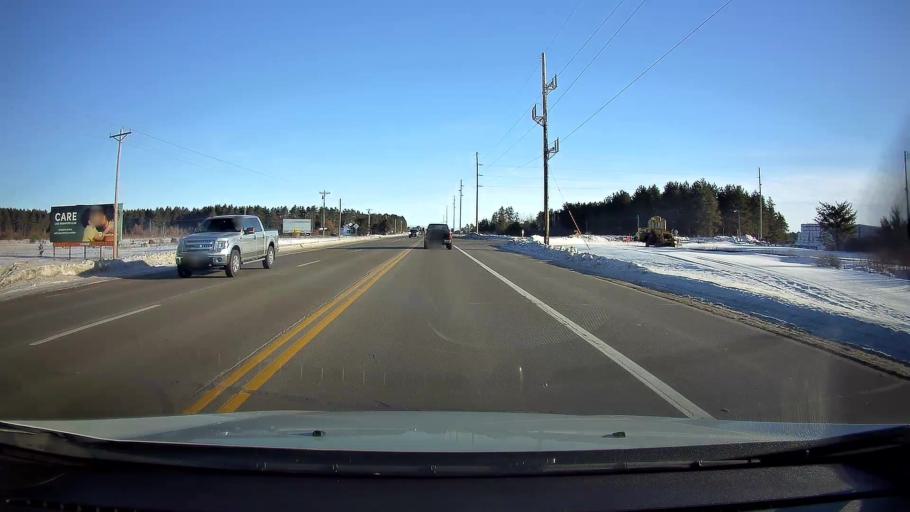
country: US
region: Wisconsin
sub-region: Sawyer County
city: Hayward
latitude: 45.9880
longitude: -91.5234
